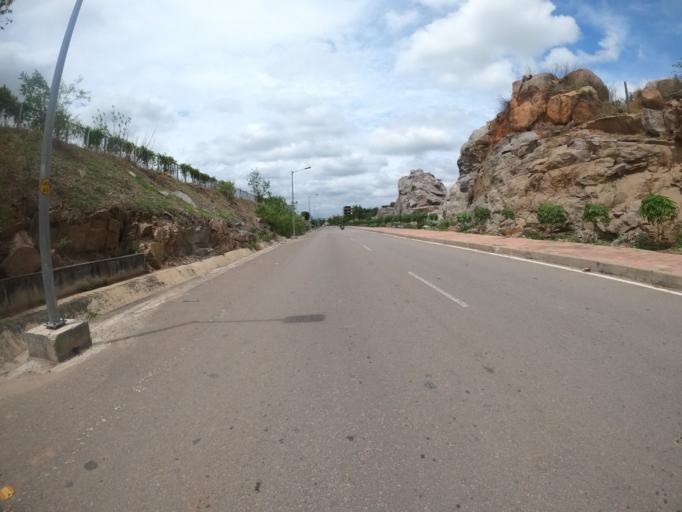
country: IN
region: Telangana
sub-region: Rangareddi
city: Sriramnagar
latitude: 17.2705
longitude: 78.3794
